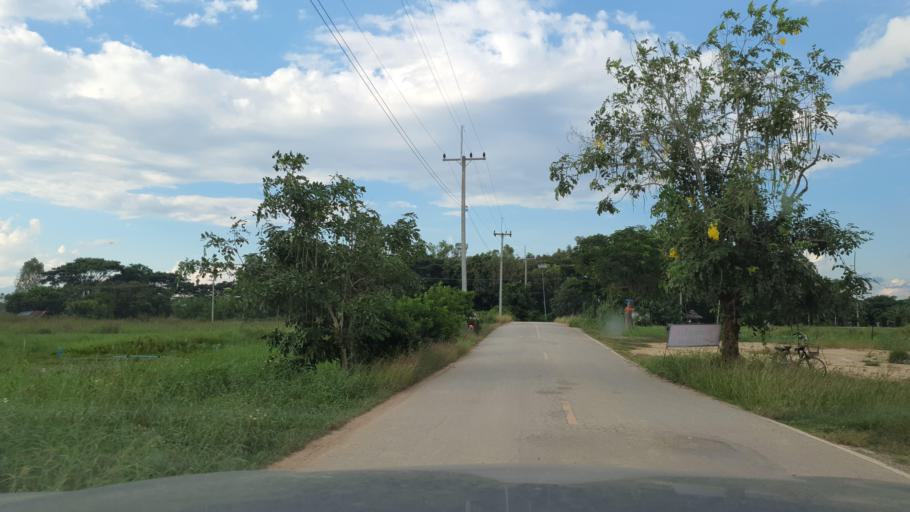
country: TH
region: Phayao
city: Phayao
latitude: 19.1915
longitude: 99.8584
